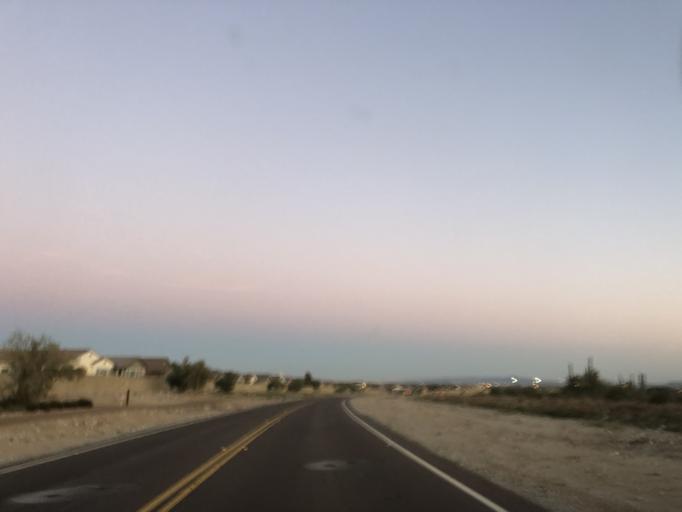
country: US
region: Arizona
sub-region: Maricopa County
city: Citrus Park
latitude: 33.5022
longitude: -112.5092
